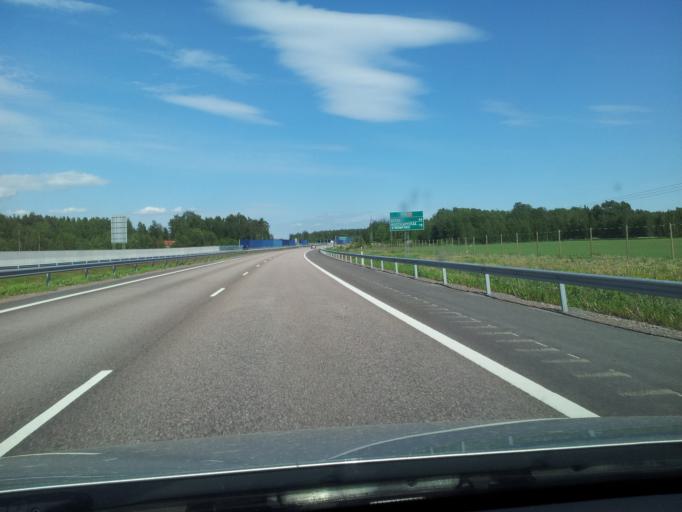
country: FI
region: Uusimaa
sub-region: Loviisa
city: Lovisa
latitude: 60.4657
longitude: 26.2140
